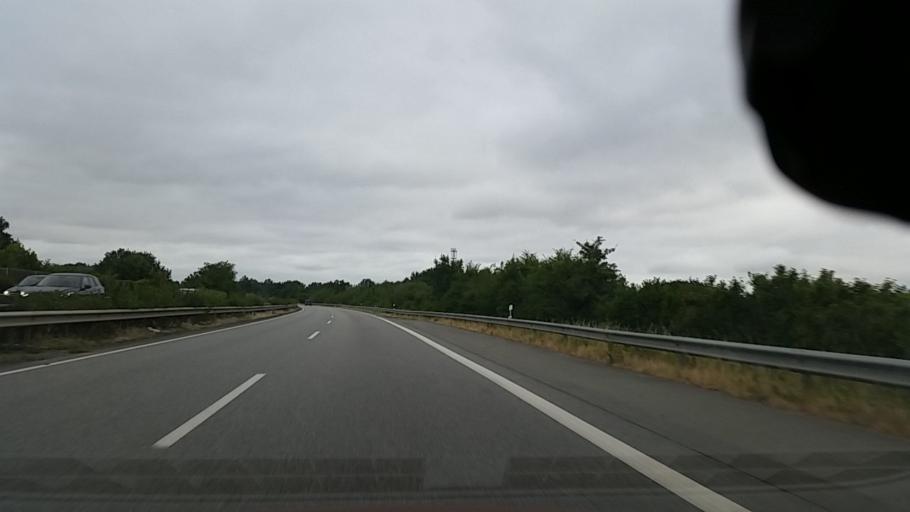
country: DE
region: Schleswig-Holstein
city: Bebensee
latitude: 53.8793
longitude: 10.3103
